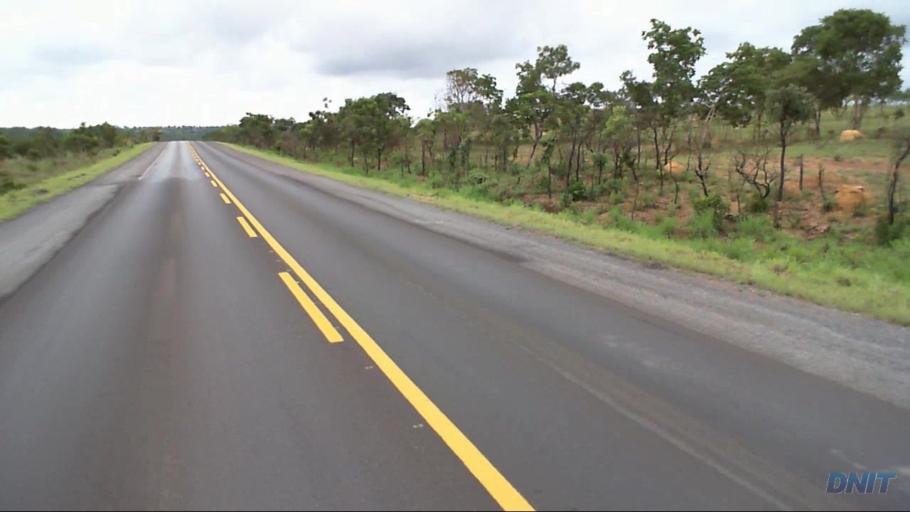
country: BR
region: Goias
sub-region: Padre Bernardo
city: Padre Bernardo
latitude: -15.2131
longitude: -48.5754
